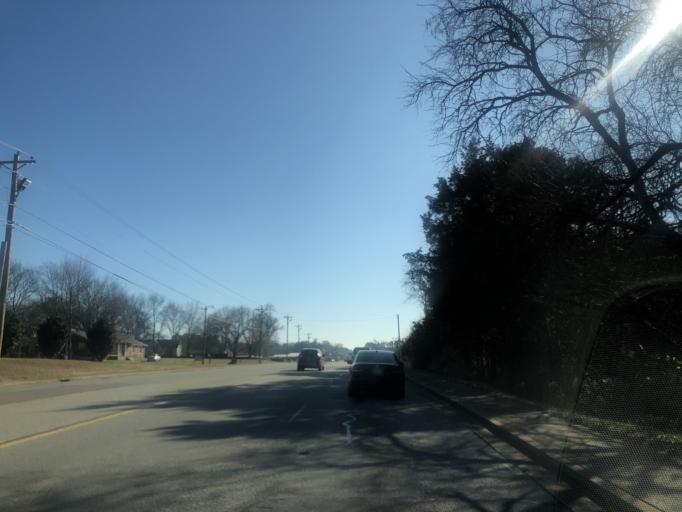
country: US
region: Tennessee
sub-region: Rutherford County
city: Smyrna
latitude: 35.9507
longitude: -86.5109
